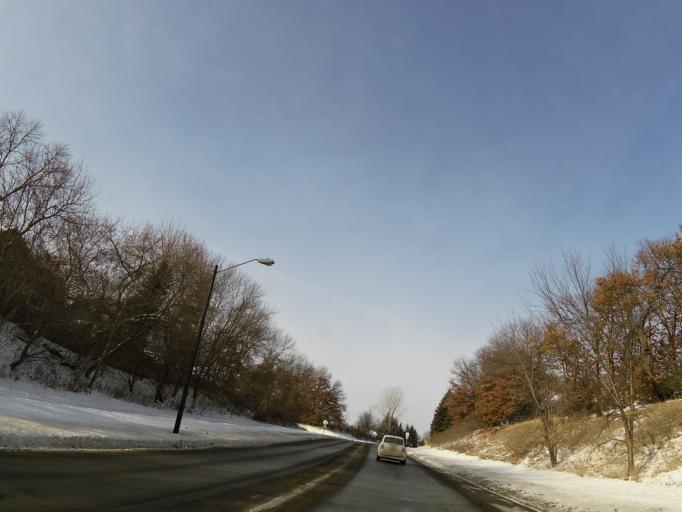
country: US
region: Minnesota
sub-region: Hennepin County
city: Eden Prairie
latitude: 44.8475
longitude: -93.4481
